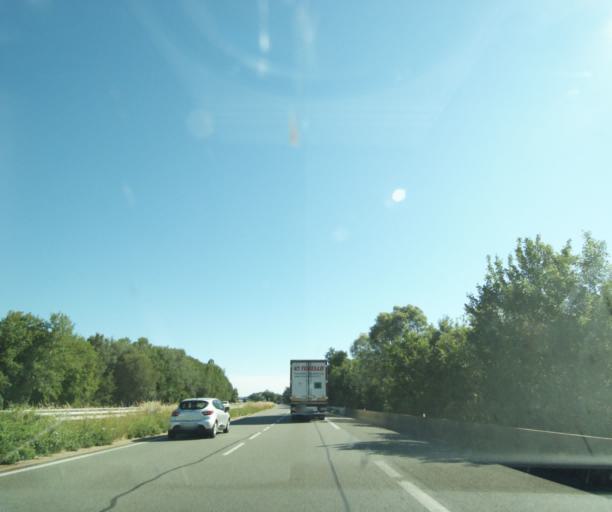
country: FR
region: Champagne-Ardenne
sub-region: Departement de la Haute-Marne
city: Avrecourt
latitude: 47.9707
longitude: 5.4938
